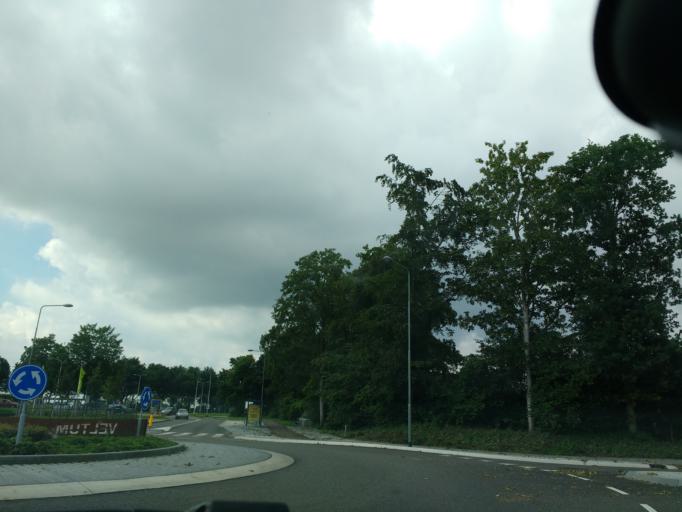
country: NL
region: Limburg
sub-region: Gemeente Venray
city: Venray
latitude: 51.5145
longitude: 5.9646
